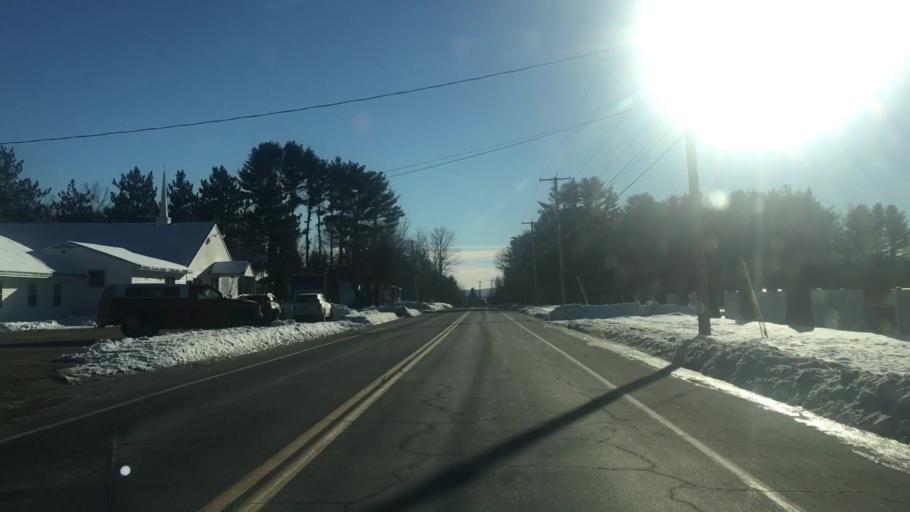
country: US
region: Maine
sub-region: Somerset County
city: Madison
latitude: 44.7859
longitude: -69.8837
